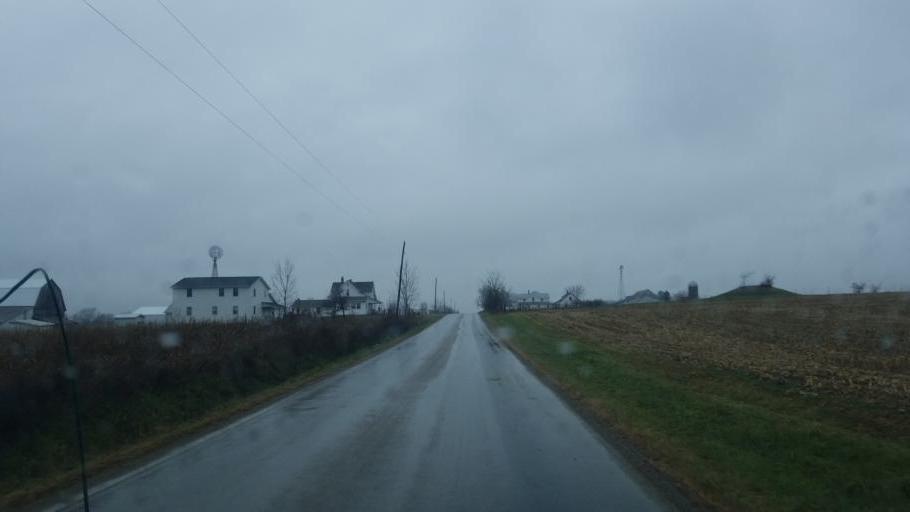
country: US
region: Indiana
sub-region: Adams County
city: Geneva
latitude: 40.6171
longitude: -84.9356
